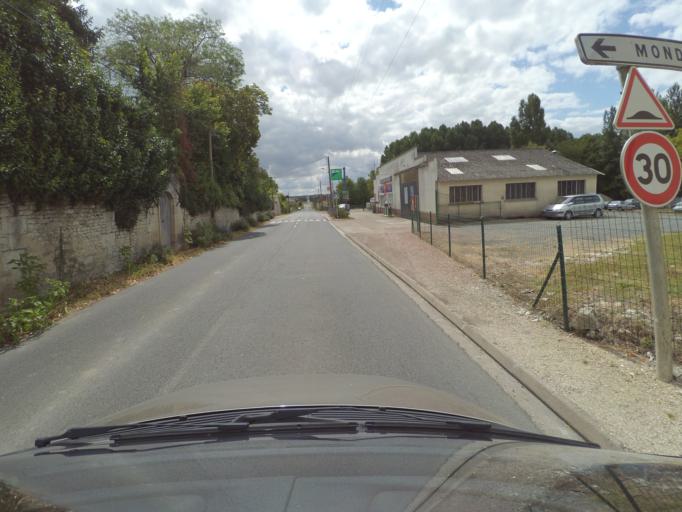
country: FR
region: Poitou-Charentes
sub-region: Departement de la Vienne
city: Saint-Gervais-les-Trois-Clochers
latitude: 46.9471
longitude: 0.4155
